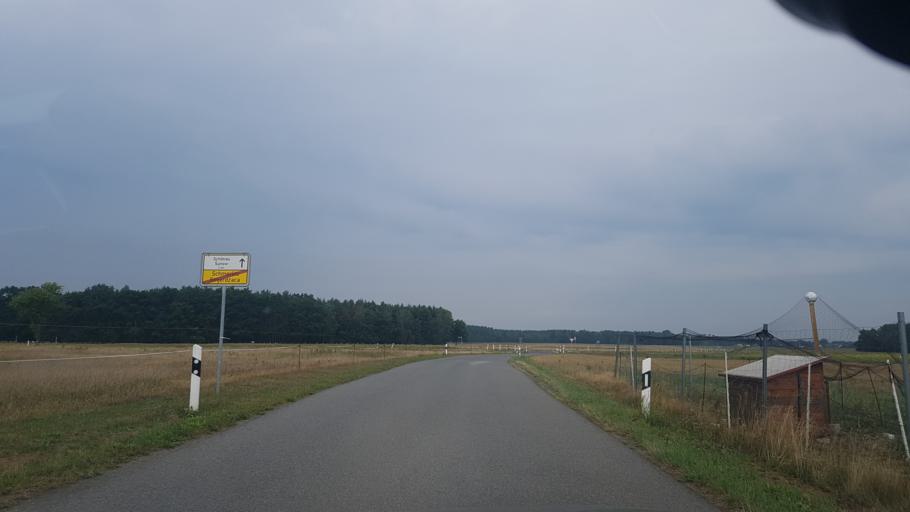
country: DE
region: Saxony
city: Rackelwitz
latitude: 51.3040
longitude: 14.2145
